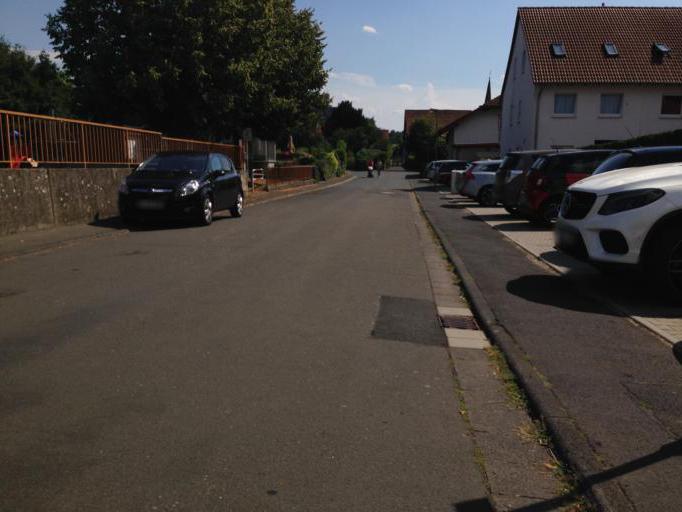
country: DE
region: Hesse
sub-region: Regierungsbezirk Giessen
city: Heuchelheim
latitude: 50.6255
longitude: 8.6342
